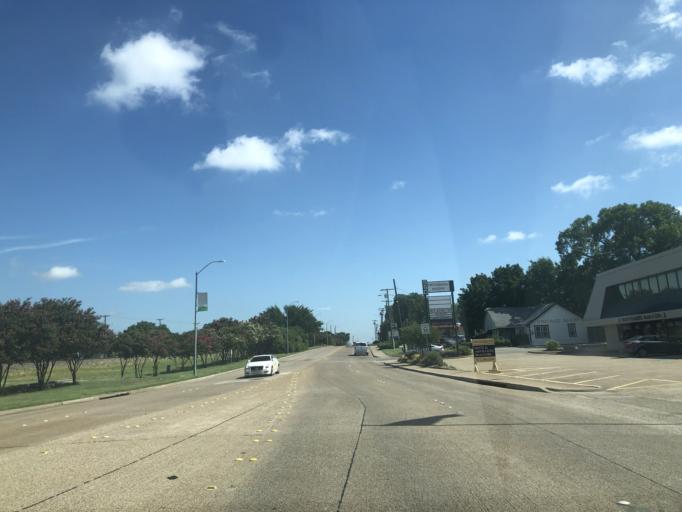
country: US
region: Texas
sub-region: Dallas County
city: Duncanville
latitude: 32.6567
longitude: -96.9076
